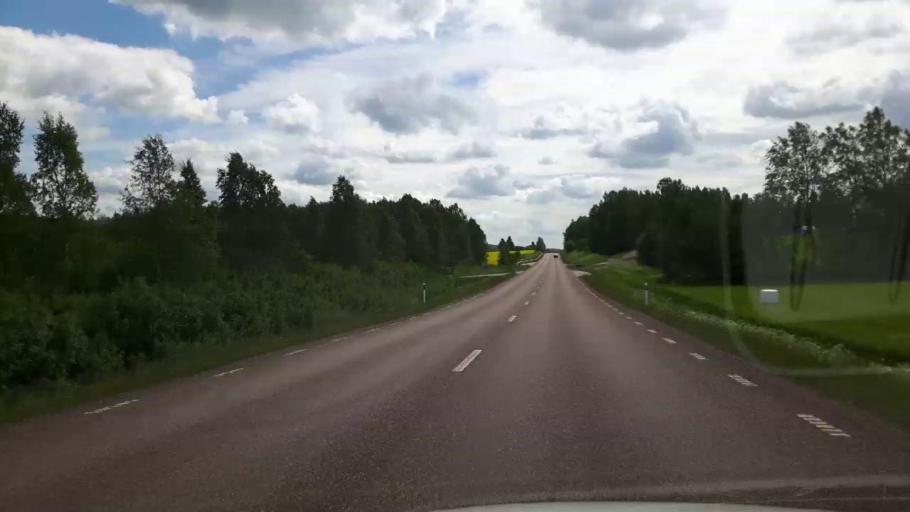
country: SE
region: Dalarna
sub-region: Hedemora Kommun
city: Langshyttan
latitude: 60.3824
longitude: 15.9081
